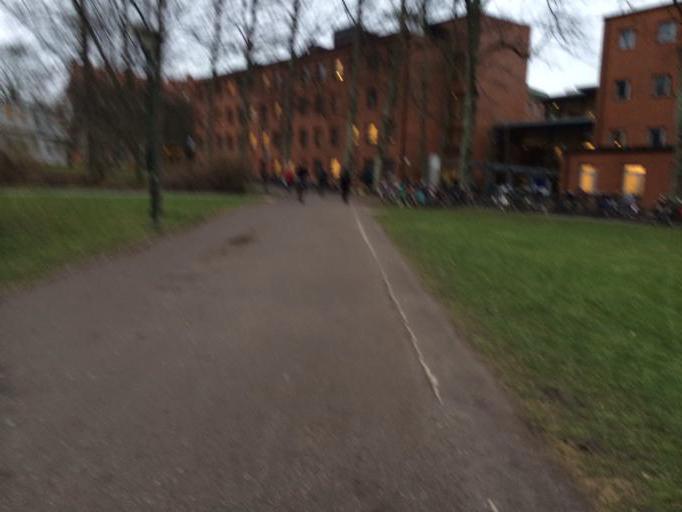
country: SE
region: Skane
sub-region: Lunds Kommun
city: Lund
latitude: 55.7088
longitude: 13.1977
